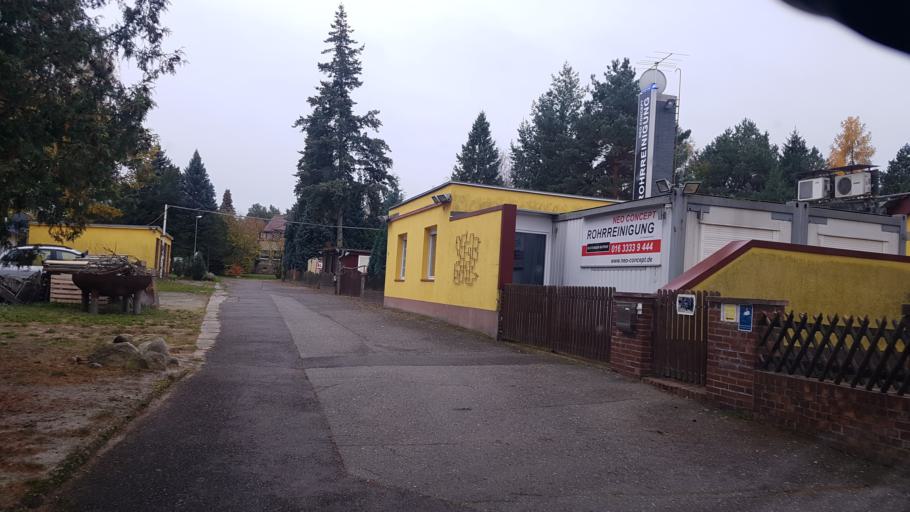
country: DE
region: Brandenburg
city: Crinitz
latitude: 51.7373
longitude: 13.7565
